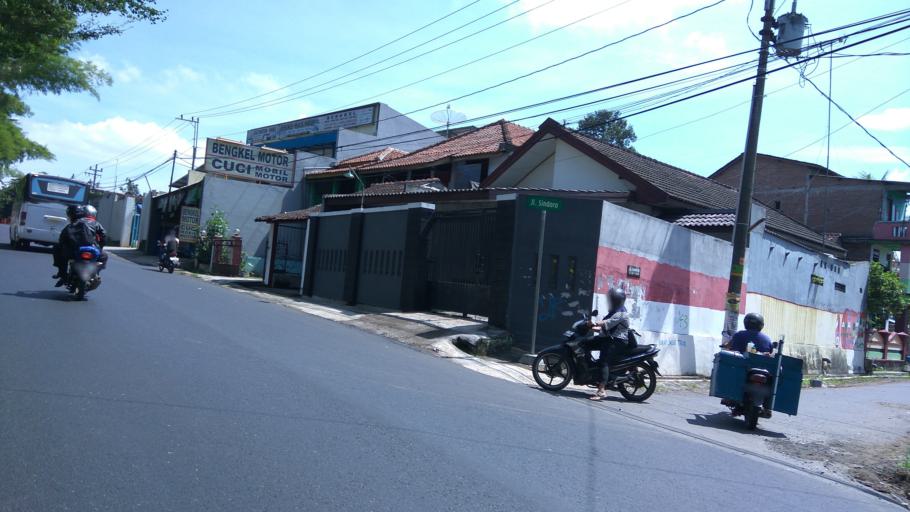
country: ID
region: Central Java
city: Ungaran
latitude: -7.1152
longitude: 110.4082
